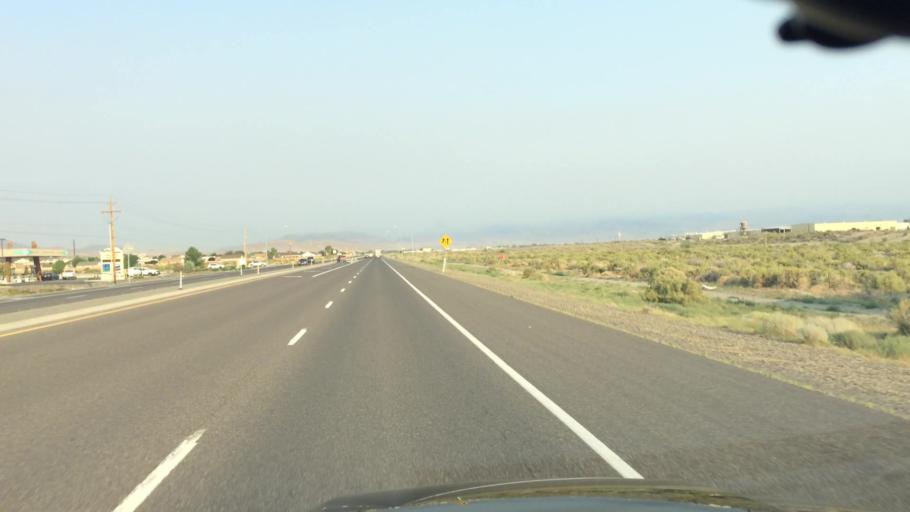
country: US
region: Nevada
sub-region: Lyon County
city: Fernley
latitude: 39.5981
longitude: -119.1948
